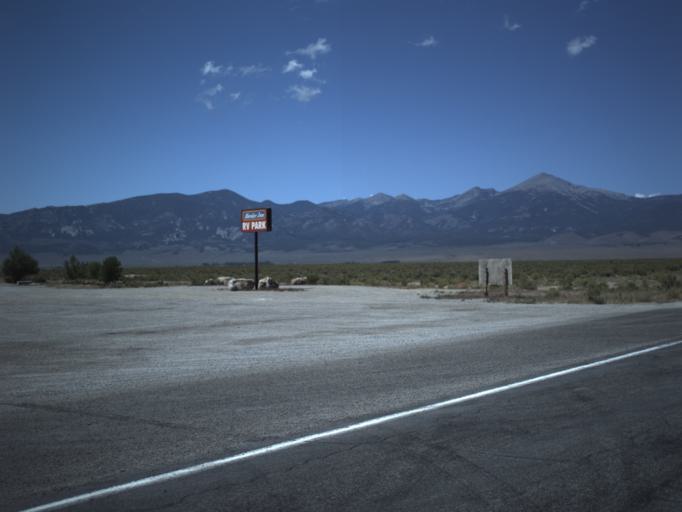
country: US
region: Nevada
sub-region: White Pine County
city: McGill
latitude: 39.0572
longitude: -114.0494
